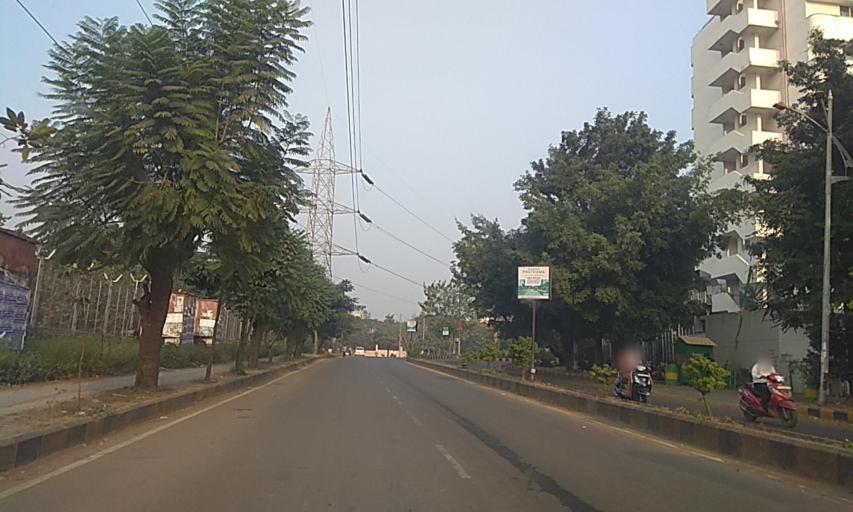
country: IN
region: Maharashtra
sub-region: Pune Division
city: Pimpri
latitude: 18.5849
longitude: 73.7343
